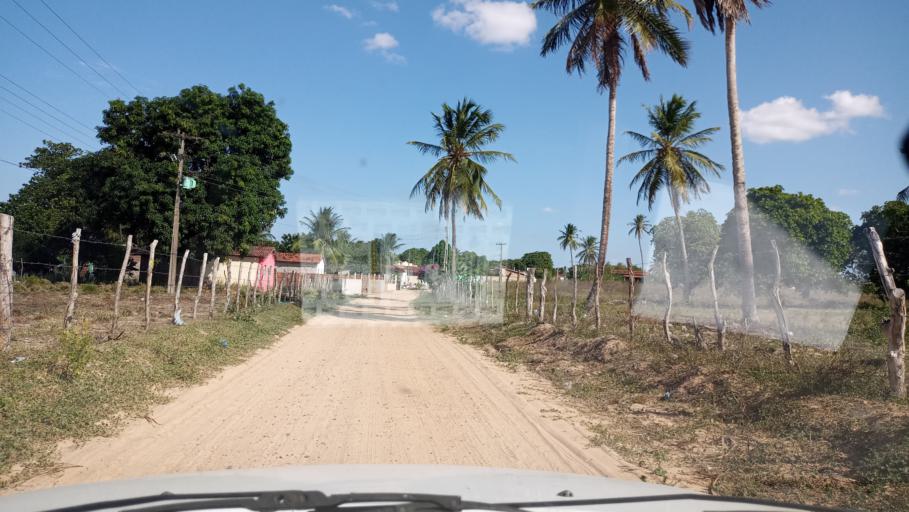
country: BR
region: Rio Grande do Norte
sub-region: Brejinho
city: Brejinho
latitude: -6.1722
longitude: -35.4690
